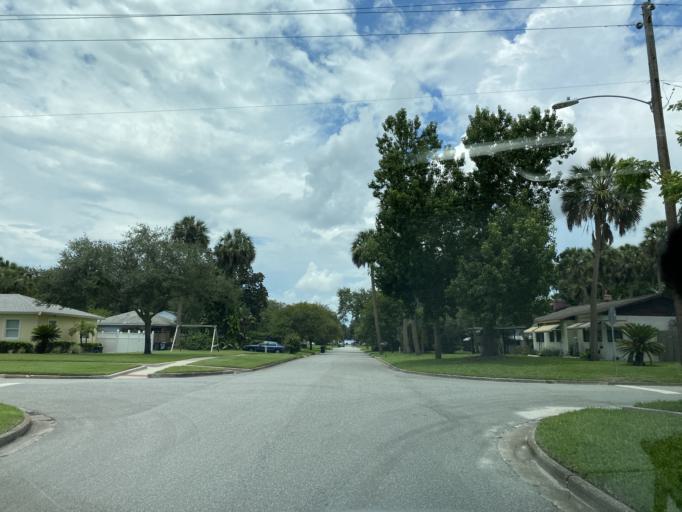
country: US
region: Florida
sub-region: Seminole County
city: Sanford
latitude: 28.8084
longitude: -81.2515
